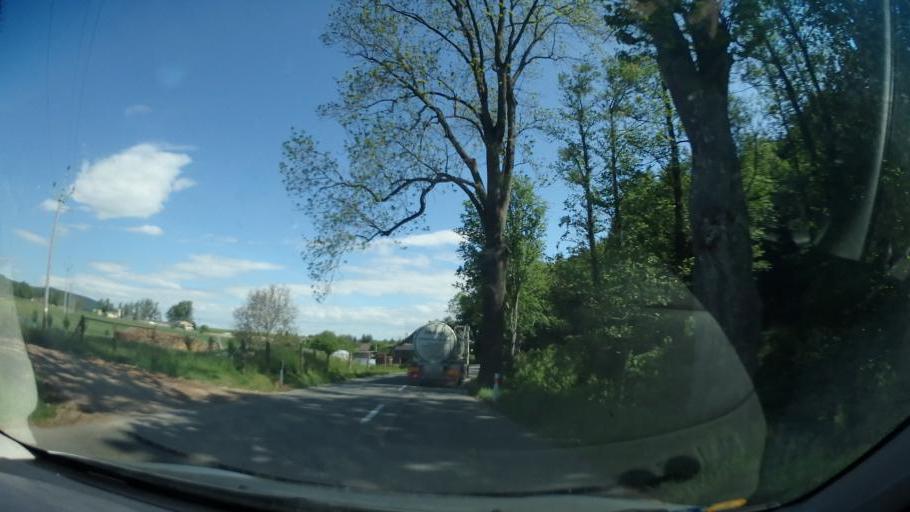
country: CZ
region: Pardubicky
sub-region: Okres Svitavy
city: Moravska Trebova
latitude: 49.6924
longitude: 16.6311
